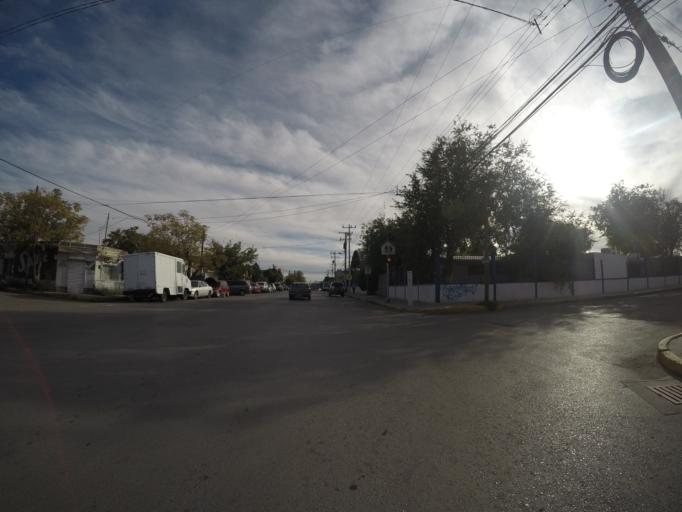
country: MX
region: Chihuahua
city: Ciudad Juarez
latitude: 31.7284
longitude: -106.4279
